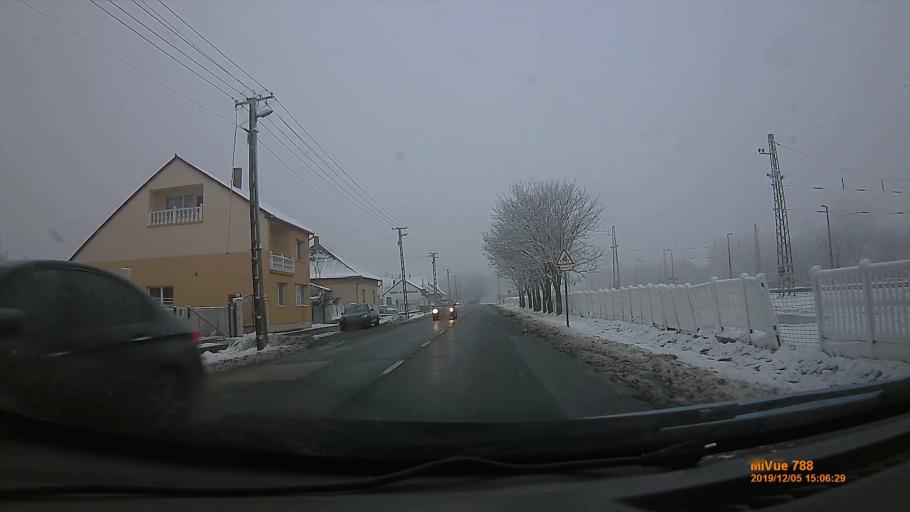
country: HU
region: Szabolcs-Szatmar-Bereg
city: Rakamaz
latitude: 48.1181
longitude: 21.4772
